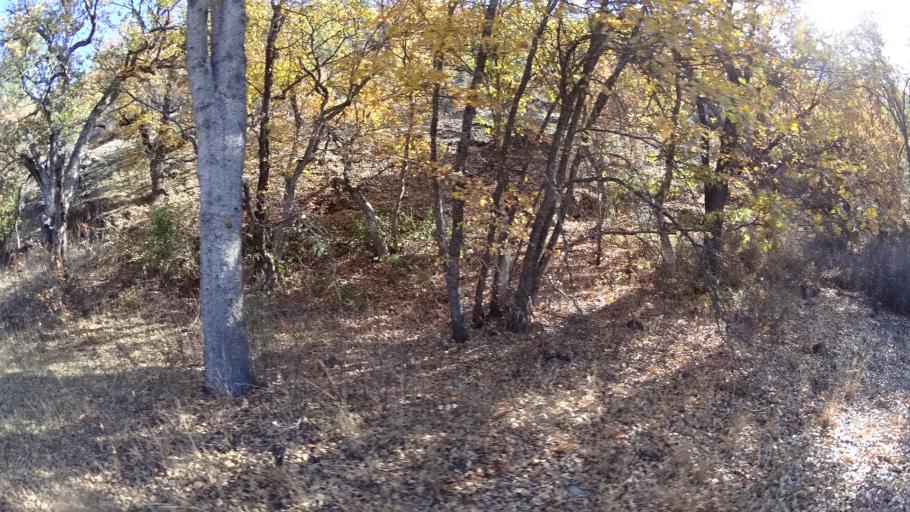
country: US
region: California
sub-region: Siskiyou County
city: Yreka
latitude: 41.8649
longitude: -122.8177
